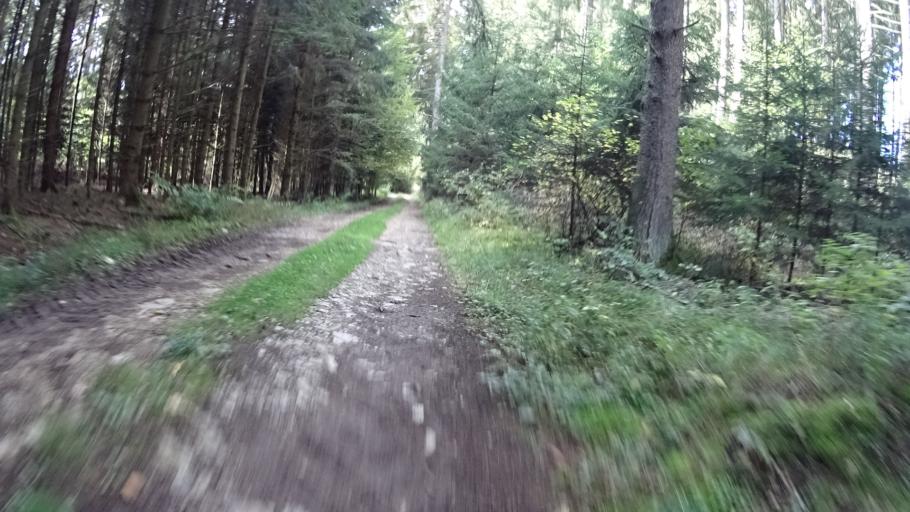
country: DE
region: Bavaria
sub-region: Upper Bavaria
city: Bohmfeld
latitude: 48.8826
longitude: 11.3781
